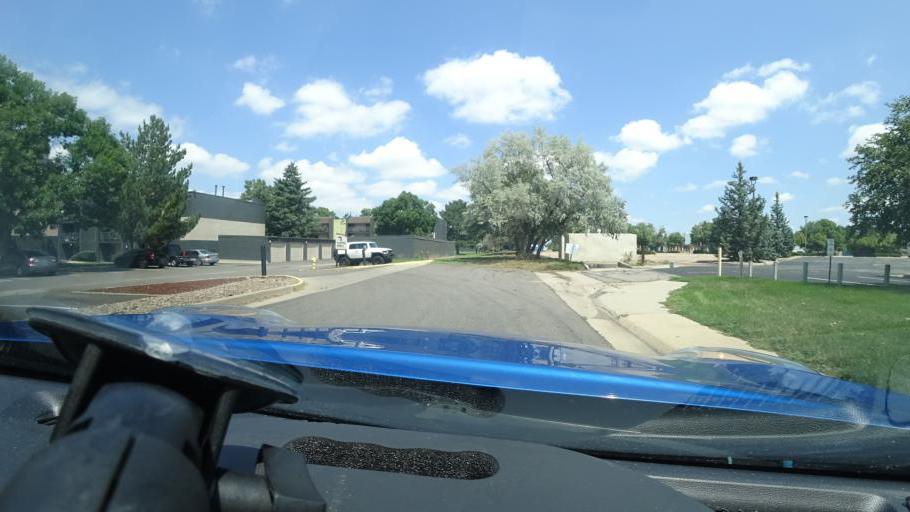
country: US
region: Colorado
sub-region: Adams County
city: Aurora
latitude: 39.7124
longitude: -104.8565
